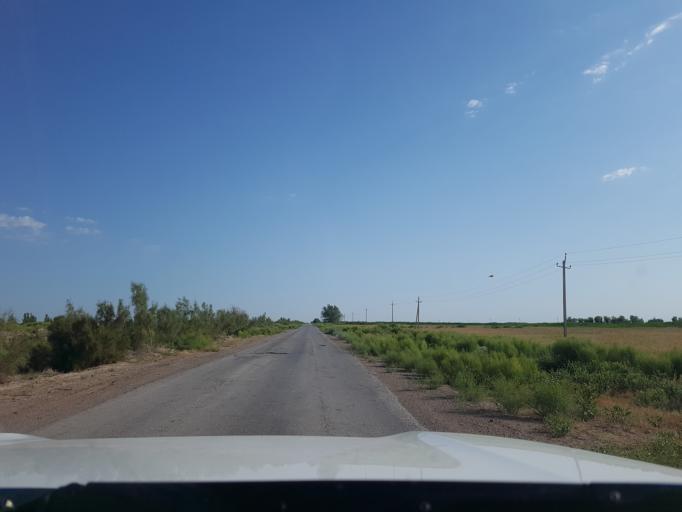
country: TM
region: Dasoguz
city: Koeneuergench
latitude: 41.9114
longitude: 58.7099
